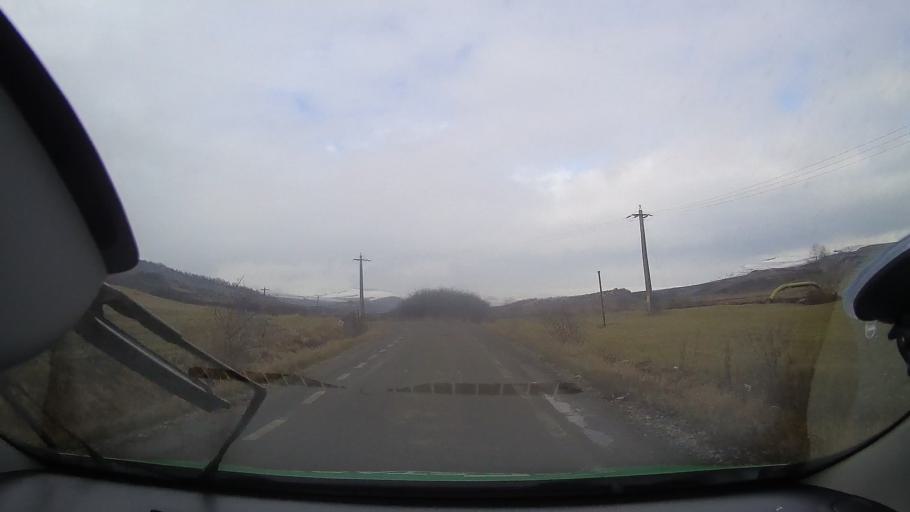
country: RO
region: Mures
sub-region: Comuna Atintis
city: Atintis
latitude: 46.4048
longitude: 24.0880
